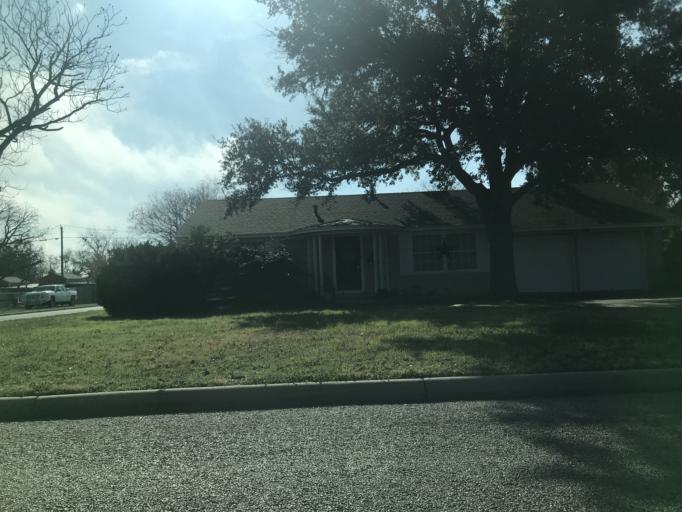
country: US
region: Texas
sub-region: Tom Green County
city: San Angelo
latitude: 31.4442
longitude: -100.4628
